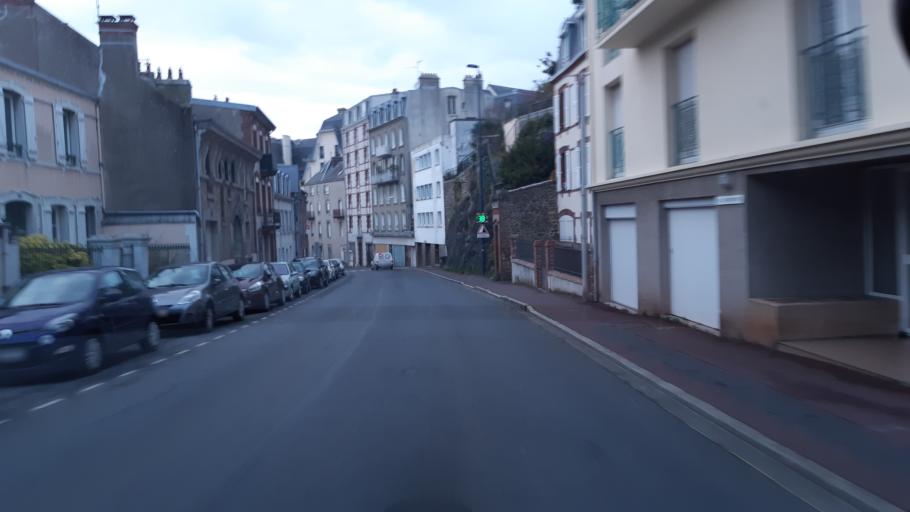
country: FR
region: Lower Normandy
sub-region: Departement de la Manche
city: Granville
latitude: 48.8390
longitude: -1.5954
